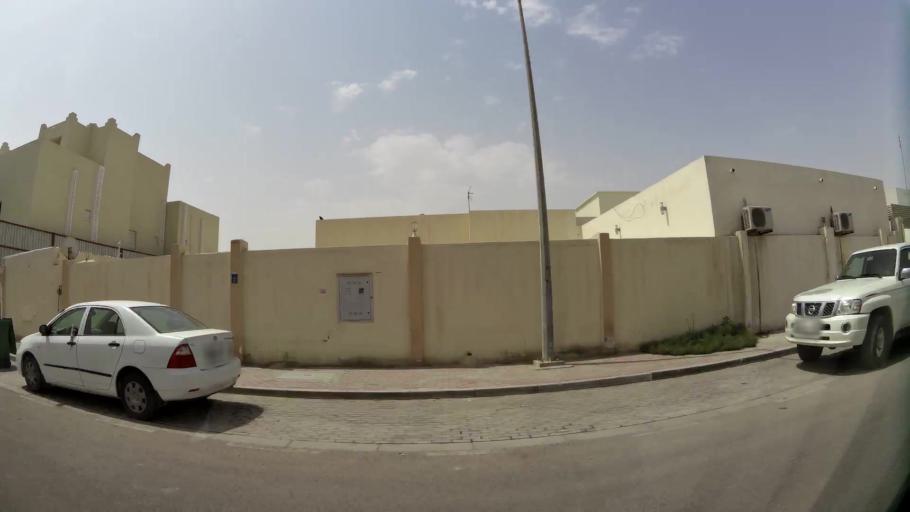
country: QA
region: Baladiyat ar Rayyan
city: Ar Rayyan
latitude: 25.2442
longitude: 51.4269
